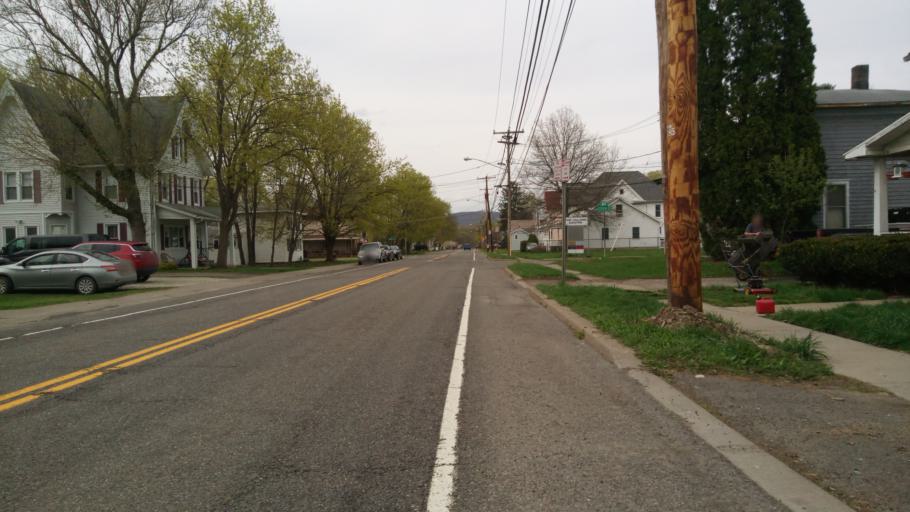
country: US
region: New York
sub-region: Chemung County
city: Southport
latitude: 42.0119
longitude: -76.7285
